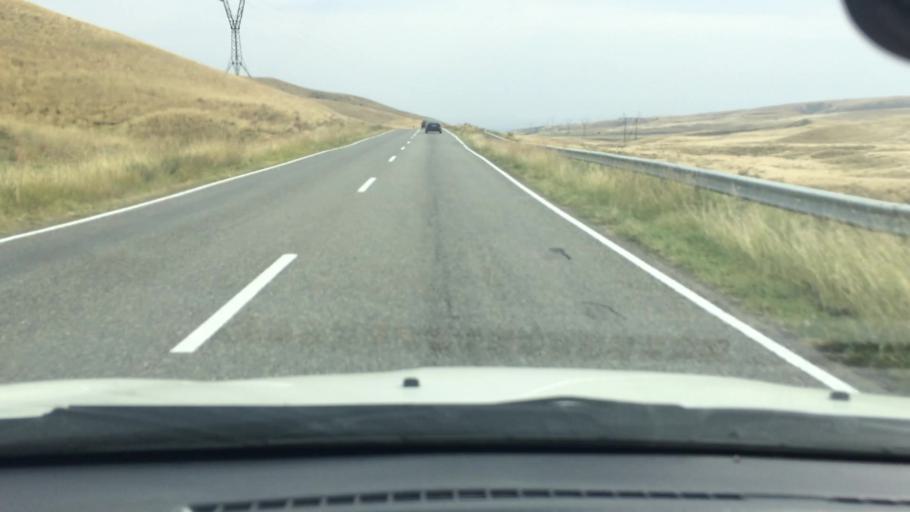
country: GE
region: Kvemo Kartli
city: Rust'avi
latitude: 41.5088
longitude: 44.9499
